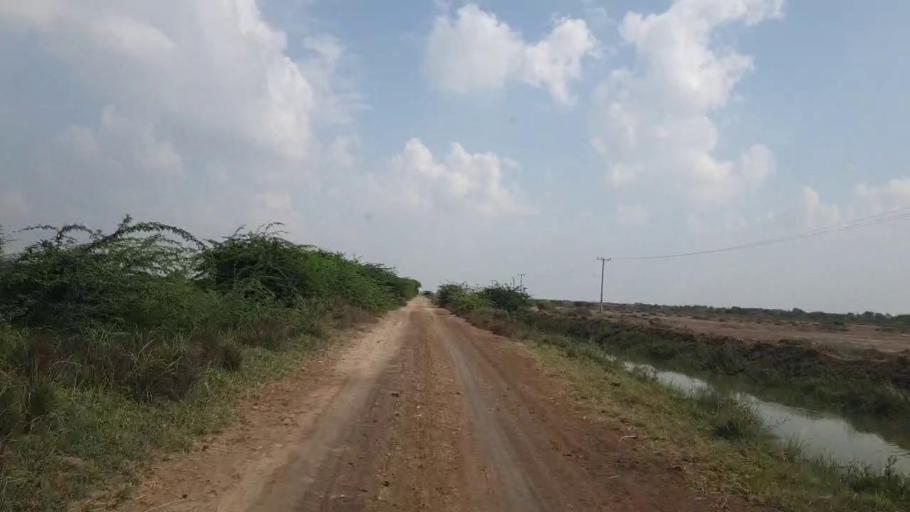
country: PK
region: Sindh
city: Badin
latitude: 24.5328
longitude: 68.6232
